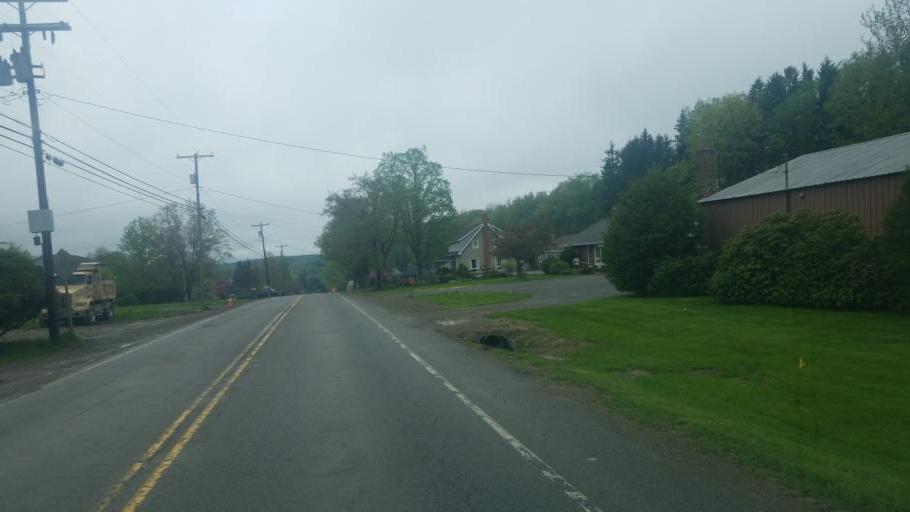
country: US
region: Pennsylvania
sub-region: McKean County
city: Kane
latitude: 41.6454
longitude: -78.8139
